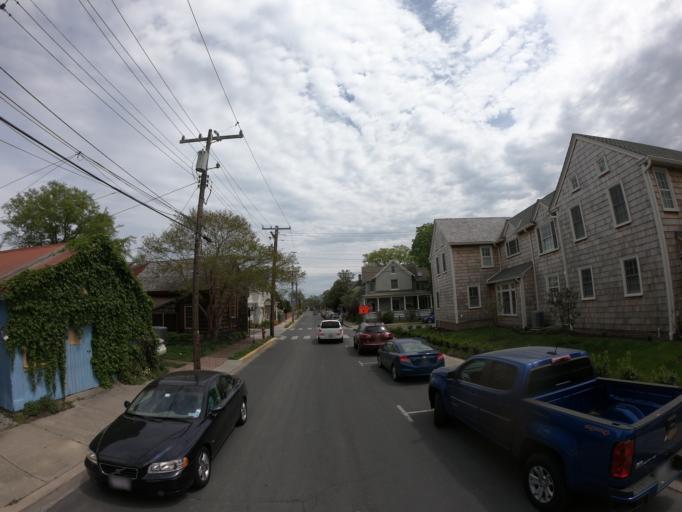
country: US
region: Delaware
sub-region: Sussex County
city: Lewes
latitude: 38.7756
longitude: -75.1420
